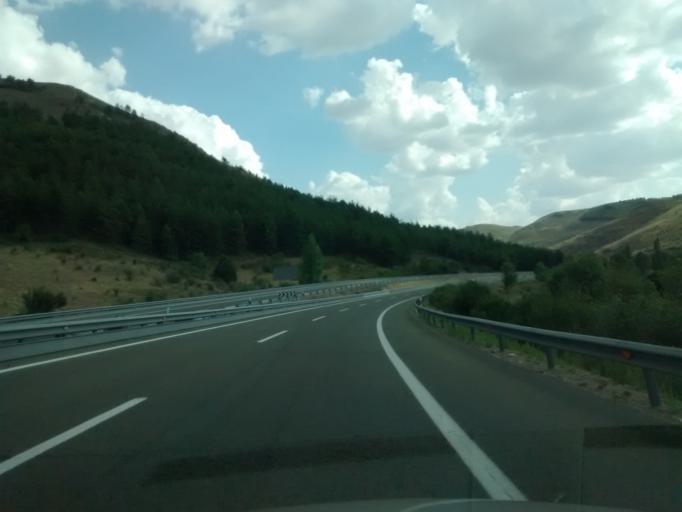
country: ES
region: Castille and Leon
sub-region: Provincia de Soria
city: Medinaceli
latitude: 41.1794
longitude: -2.3982
